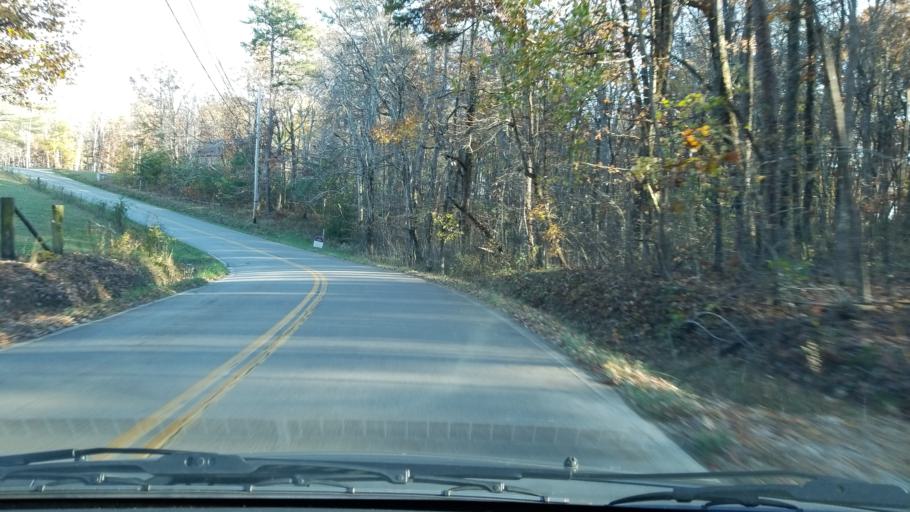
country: US
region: Tennessee
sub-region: Hamilton County
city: Falling Water
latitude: 35.2187
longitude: -85.2757
